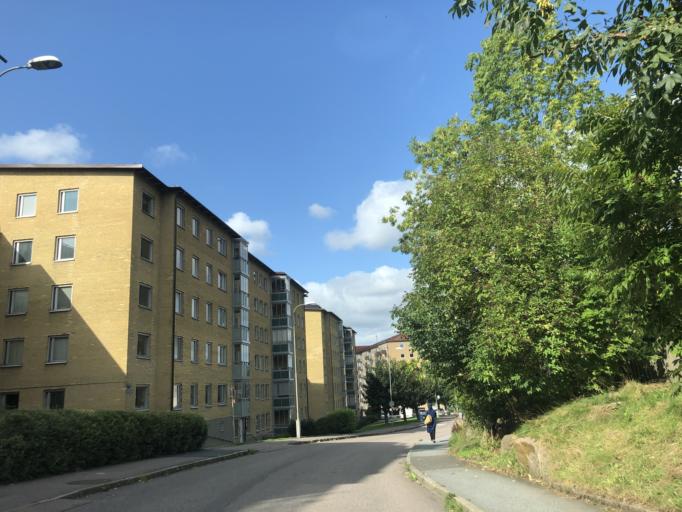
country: SE
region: Vaestra Goetaland
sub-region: Goteborg
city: Goeteborg
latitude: 57.7183
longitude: 11.9381
